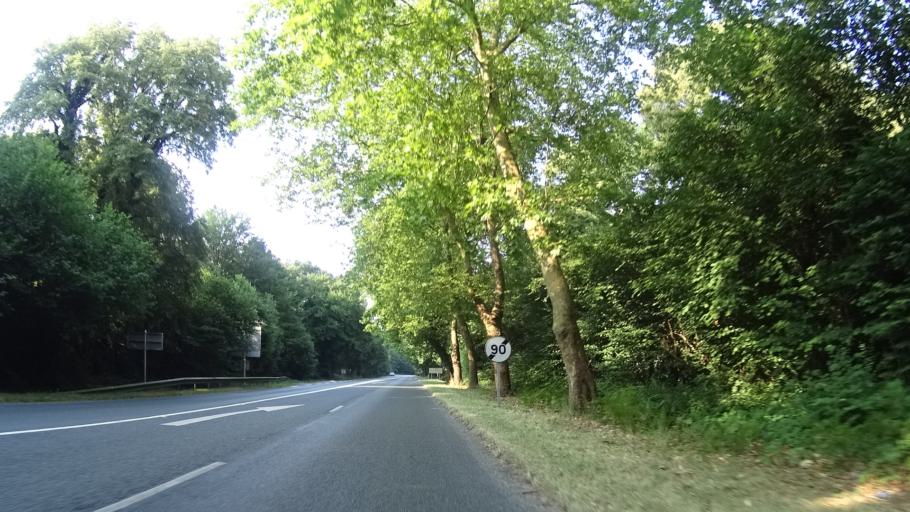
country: FR
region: Ile-de-France
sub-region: Departement du Val-d'Oise
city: Chaumontel
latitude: 49.1371
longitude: 2.4369
